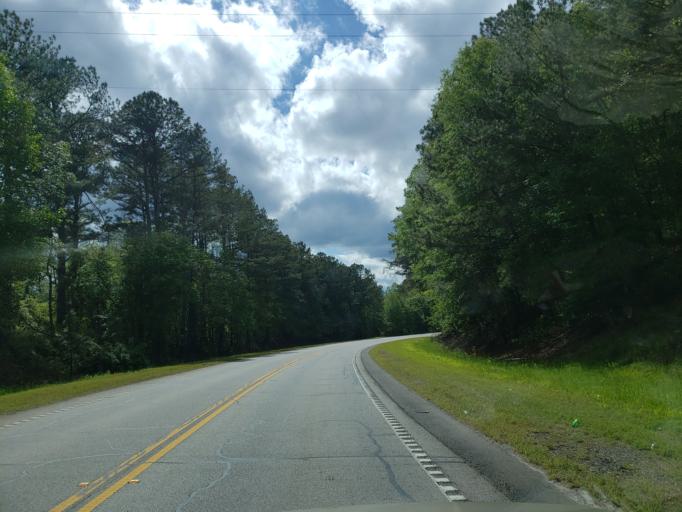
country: US
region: Georgia
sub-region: Haralson County
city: Tallapoosa
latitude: 33.7402
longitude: -85.3321
